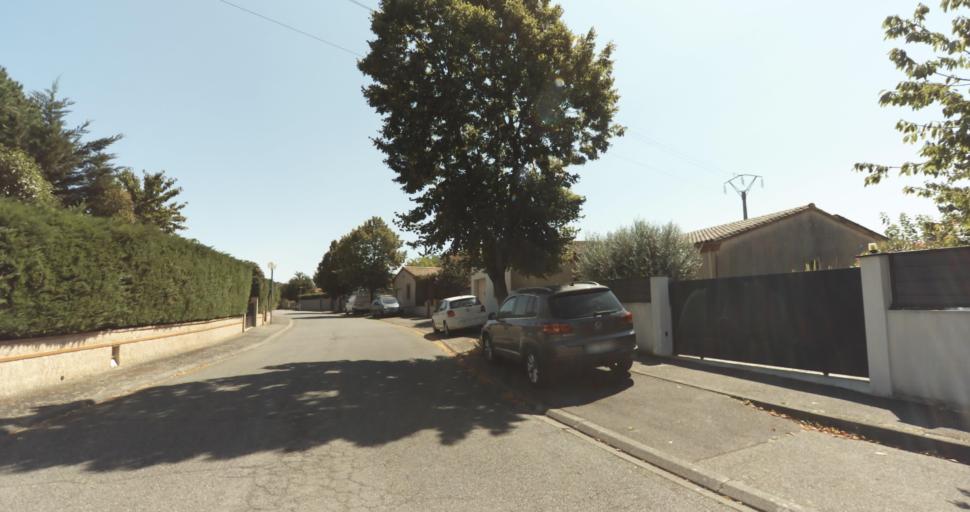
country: FR
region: Midi-Pyrenees
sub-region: Departement de la Haute-Garonne
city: L'Union
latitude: 43.6494
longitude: 1.4922
